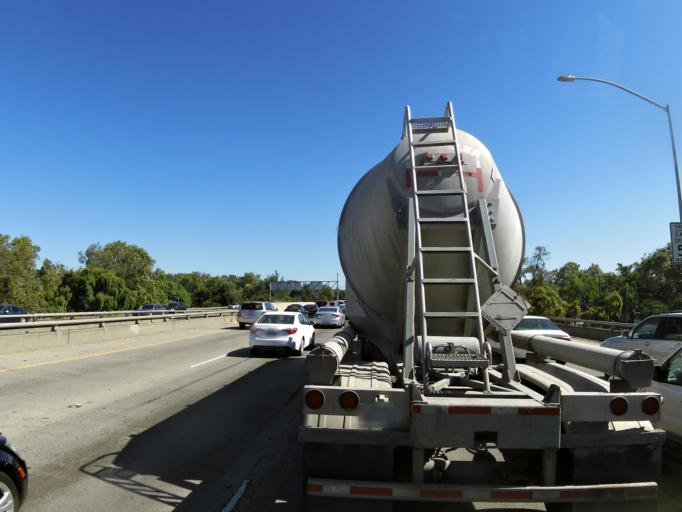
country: US
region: California
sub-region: Sacramento County
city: Sacramento
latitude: 38.5775
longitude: -121.4652
